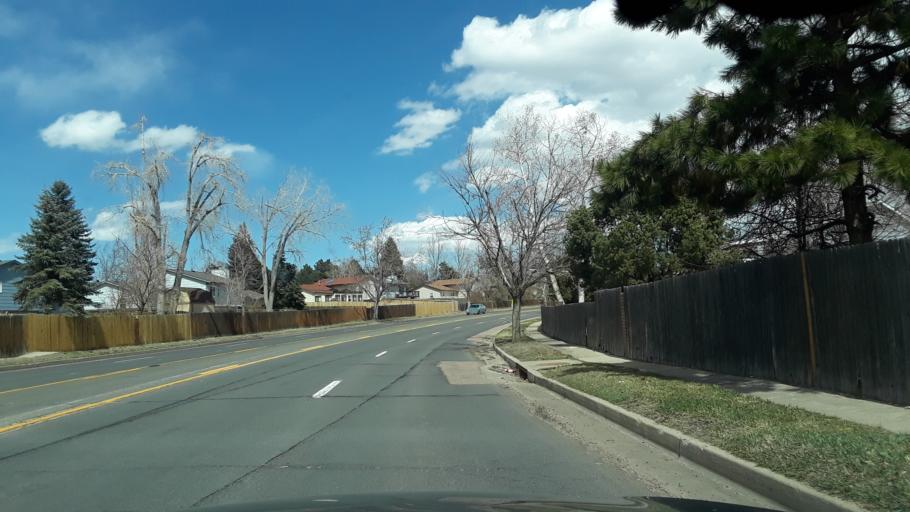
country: US
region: Colorado
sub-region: El Paso County
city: Black Forest
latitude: 38.9423
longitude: -104.7608
